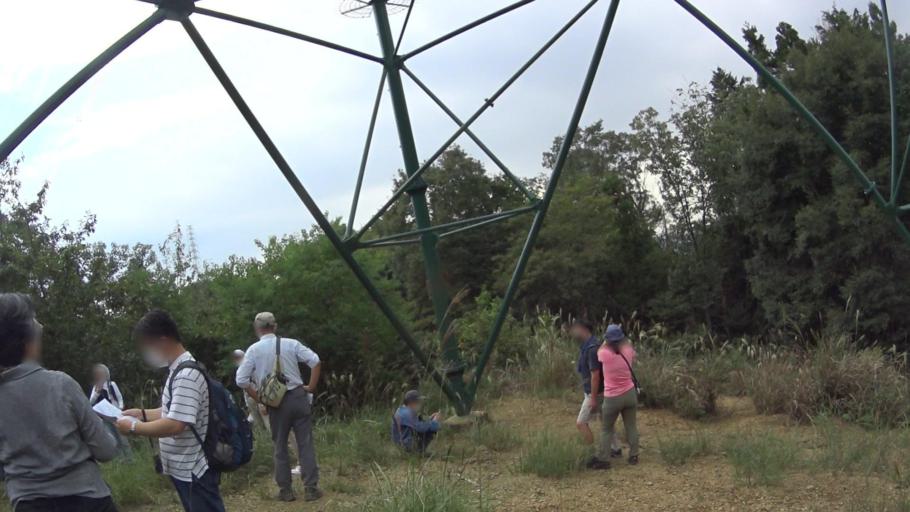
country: JP
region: Gifu
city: Tarui
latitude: 35.2899
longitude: 136.4130
